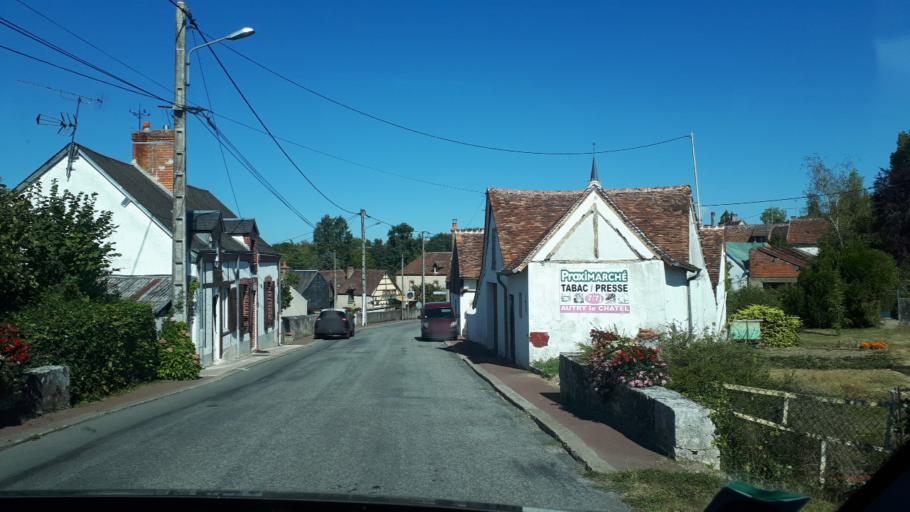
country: FR
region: Centre
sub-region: Departement du Loiret
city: Autry-le-Chatel
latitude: 47.5950
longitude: 2.6041
